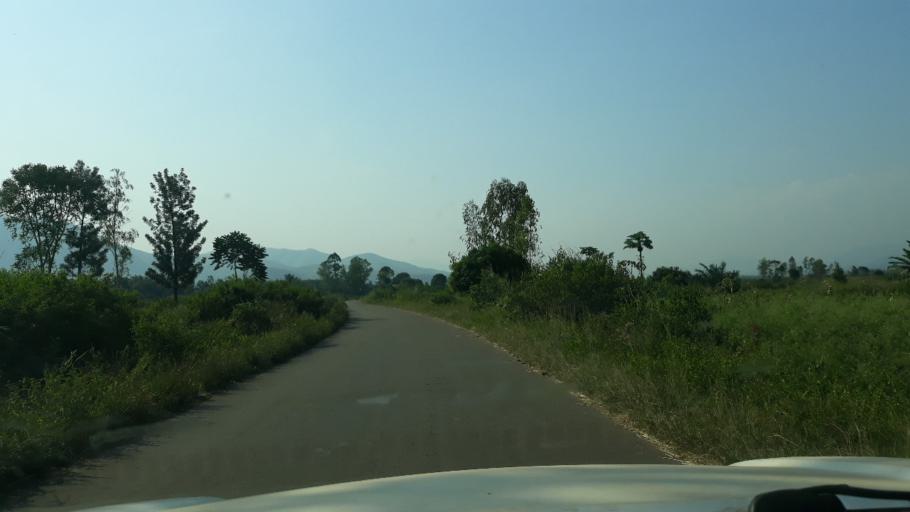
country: BI
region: Cibitoke
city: Cibitoke
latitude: -2.7696
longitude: 28.9999
